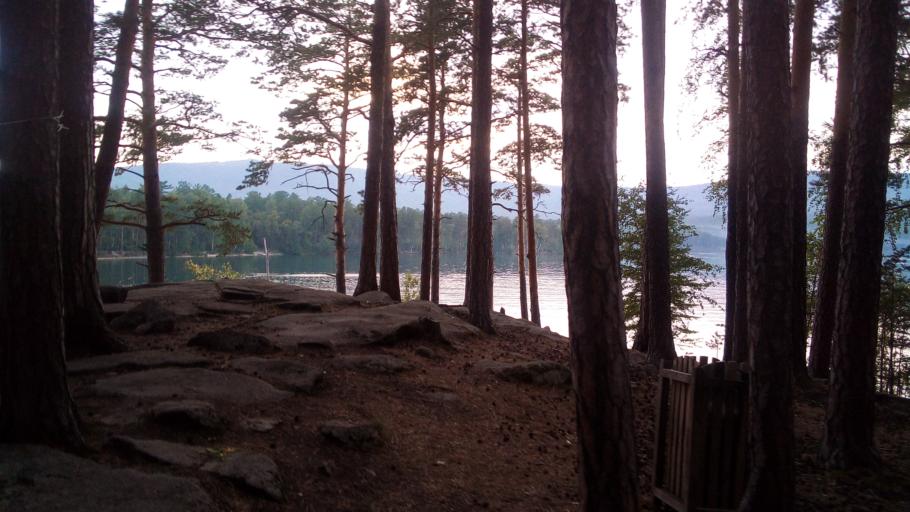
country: RU
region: Chelyabinsk
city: Turgoyak
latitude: 55.1618
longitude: 60.0303
